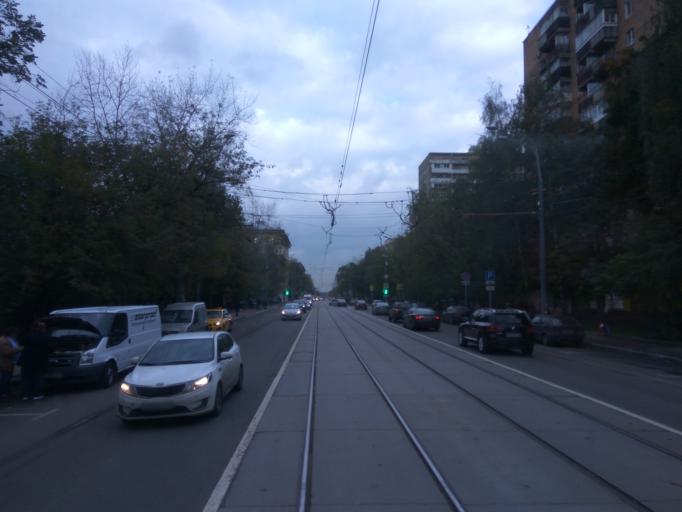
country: RU
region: Moskovskaya
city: Izmaylovo
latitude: 55.7932
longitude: 37.7922
